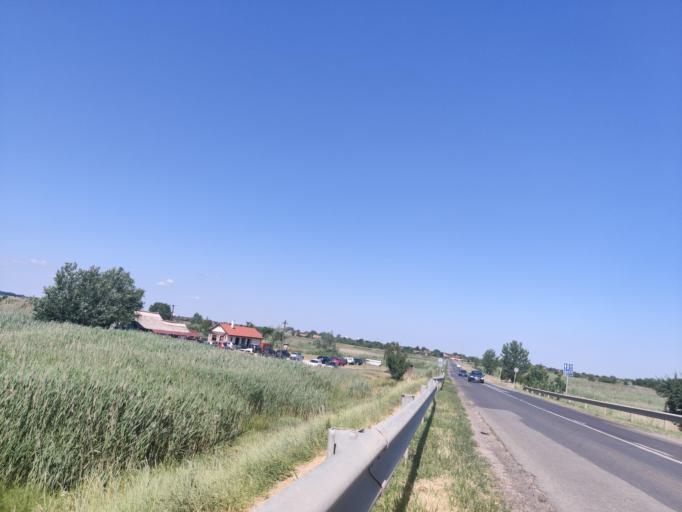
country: HU
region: Hajdu-Bihar
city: Balmazujvaros
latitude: 47.6048
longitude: 21.3772
